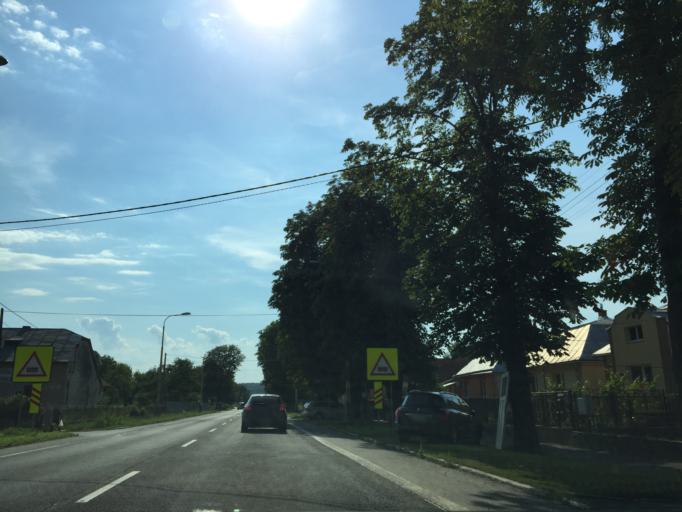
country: SK
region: Kosicky
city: Strazske
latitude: 48.8718
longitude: 21.8284
